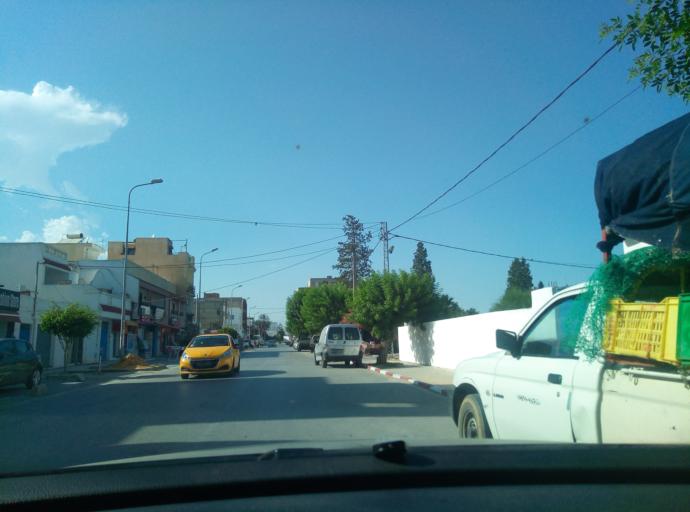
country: TN
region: Tunis
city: La Goulette
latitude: 36.8528
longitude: 10.2615
